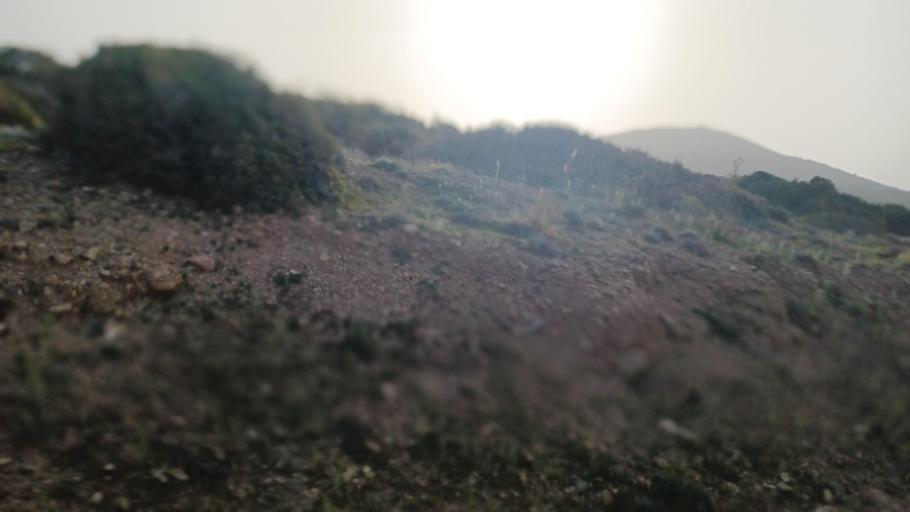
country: CY
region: Pafos
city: Pegeia
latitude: 34.9687
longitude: 32.3128
